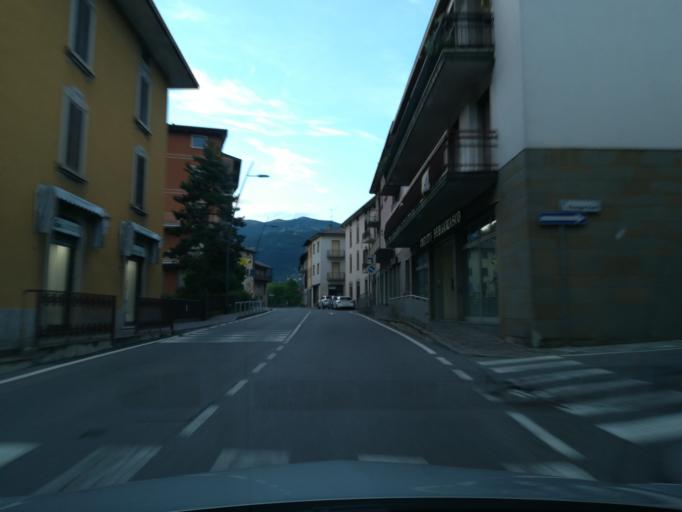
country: IT
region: Lombardy
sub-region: Provincia di Bergamo
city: Selino Basso
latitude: 45.8141
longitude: 9.5330
